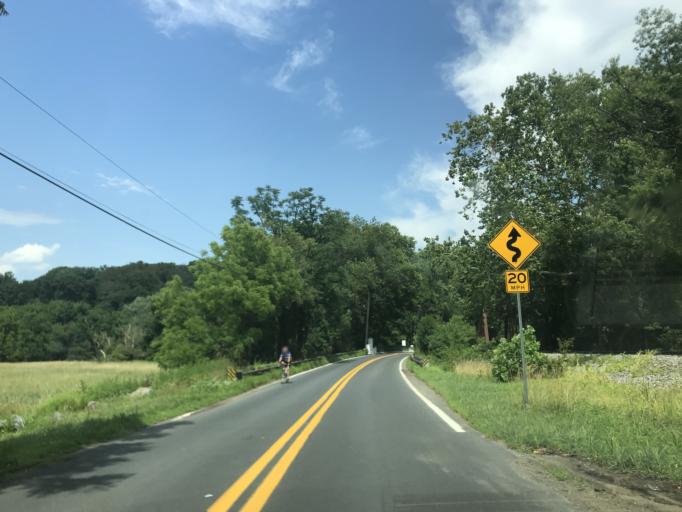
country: US
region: Delaware
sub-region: New Castle County
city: Hockessin
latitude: 39.8009
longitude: -75.6555
